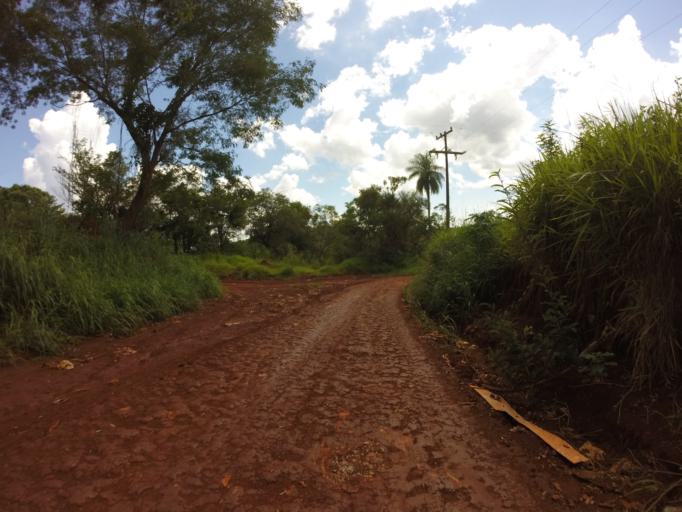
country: PY
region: Alto Parana
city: Ciudad del Este
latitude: -25.3702
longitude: -54.6782
